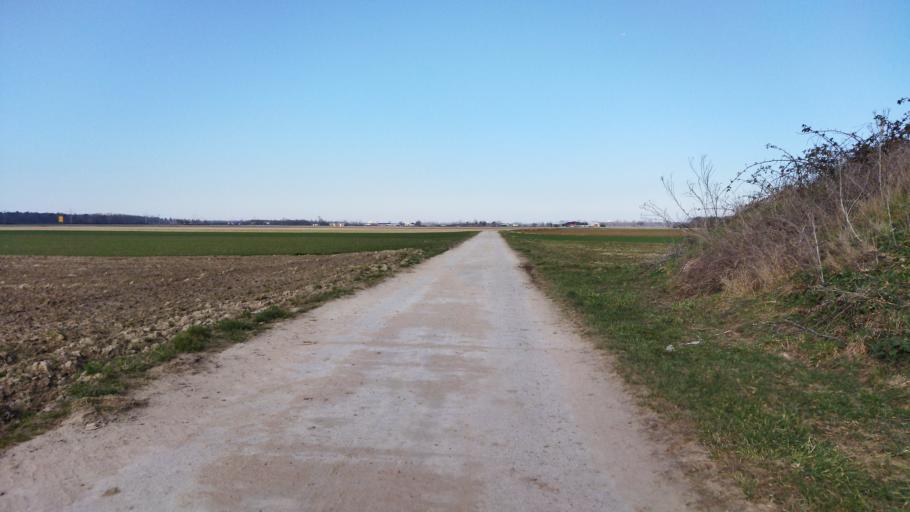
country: DE
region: Rheinland-Pfalz
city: Otterstadt
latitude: 49.3762
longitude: 8.4290
